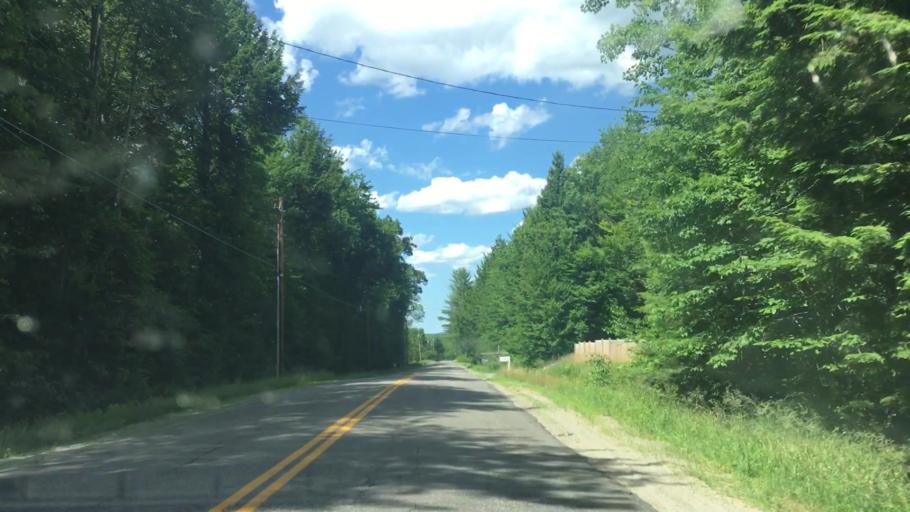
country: US
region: Maine
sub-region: Franklin County
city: Chesterville
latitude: 44.6111
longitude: -70.0823
